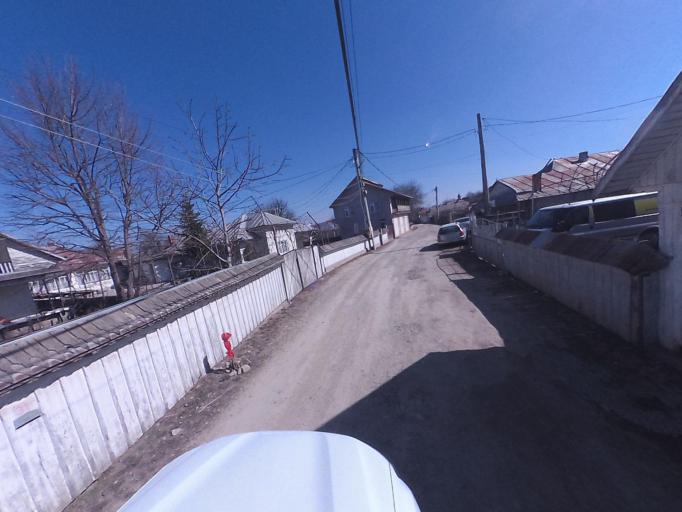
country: RO
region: Neamt
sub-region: Oras Targu Neamt
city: Humulesti
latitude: 47.1961
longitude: 26.3557
